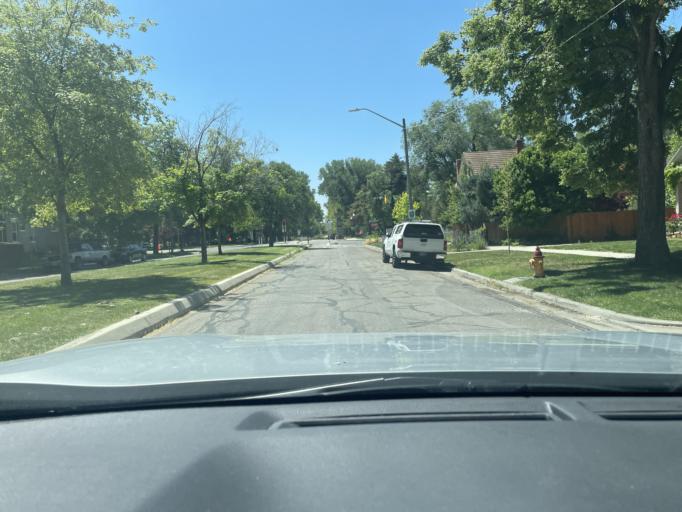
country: US
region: Utah
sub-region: Salt Lake County
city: Salt Lake City
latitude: 40.7506
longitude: -111.8739
